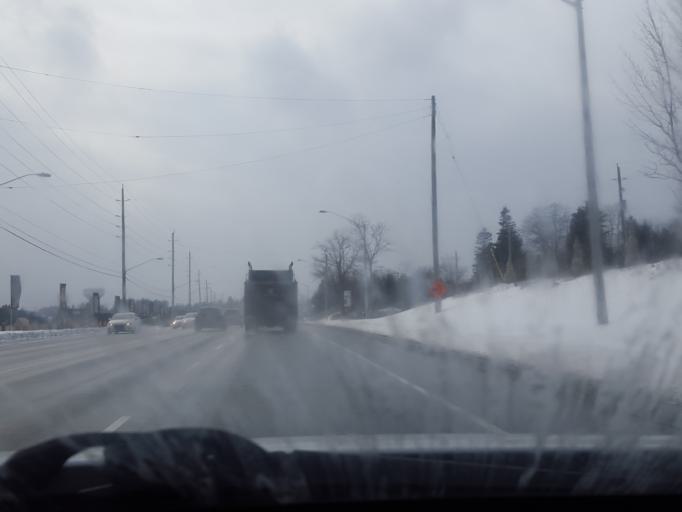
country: CA
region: Ontario
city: Newmarket
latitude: 43.9653
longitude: -79.4481
